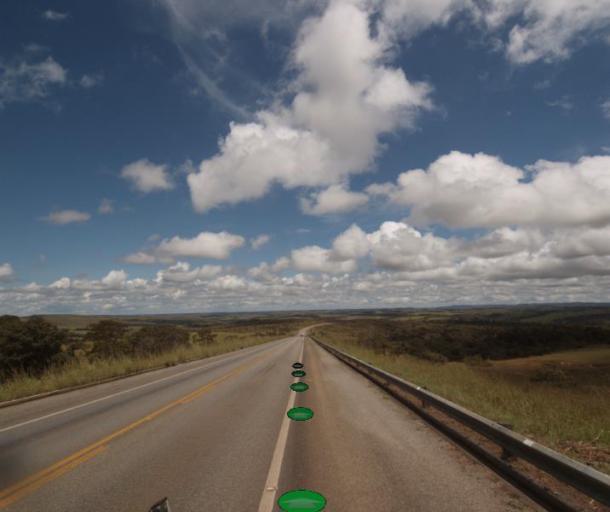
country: BR
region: Federal District
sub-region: Brasilia
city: Brasilia
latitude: -15.7566
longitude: -48.4353
